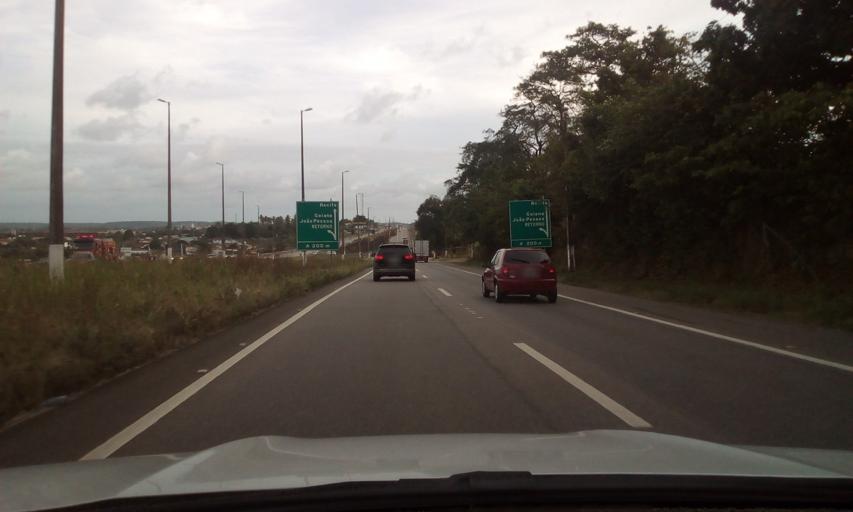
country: BR
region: Pernambuco
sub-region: Igarassu
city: Igarassu
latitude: -7.8134
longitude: -34.9185
